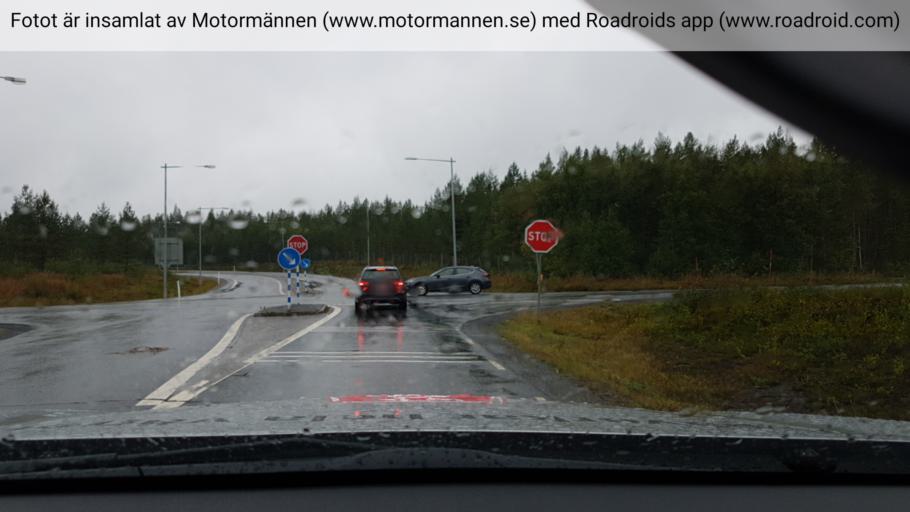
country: SE
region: Vaesterbotten
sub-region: Umea Kommun
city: Saevar
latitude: 63.8960
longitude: 20.5306
